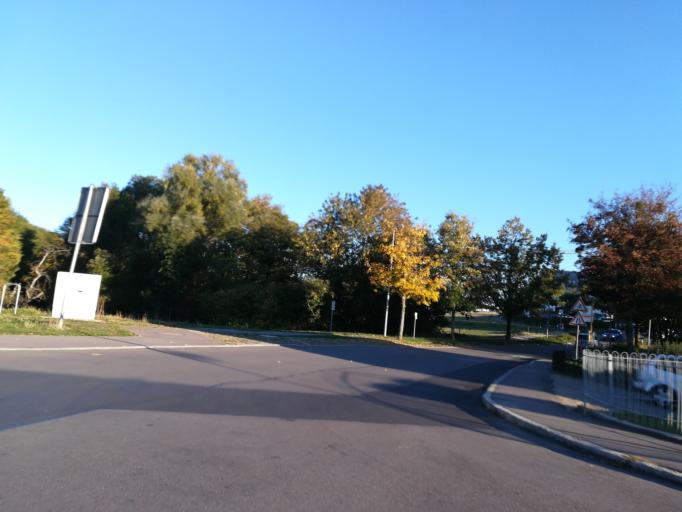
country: DE
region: Baden-Wuerttemberg
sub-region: Regierungsbezirk Stuttgart
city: Filderstadt
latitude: 48.6756
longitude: 9.2279
